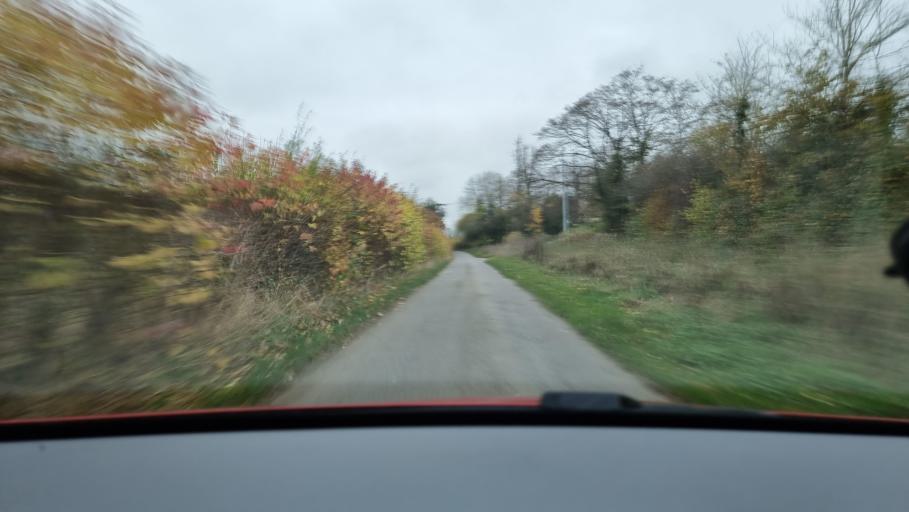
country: GB
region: England
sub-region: Oxfordshire
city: Woodstock
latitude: 51.8727
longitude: -1.3107
